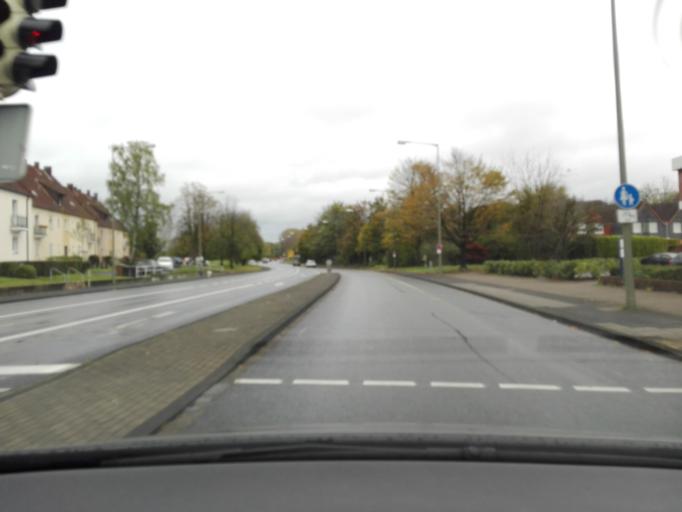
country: DE
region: North Rhine-Westphalia
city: Lunen
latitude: 51.6133
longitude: 7.5107
